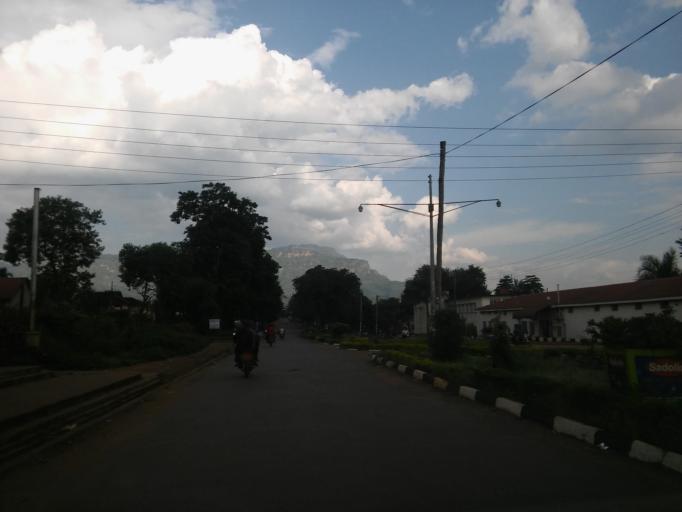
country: UG
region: Eastern Region
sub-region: Mbale District
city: Mbale
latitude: 1.0703
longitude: 34.1802
